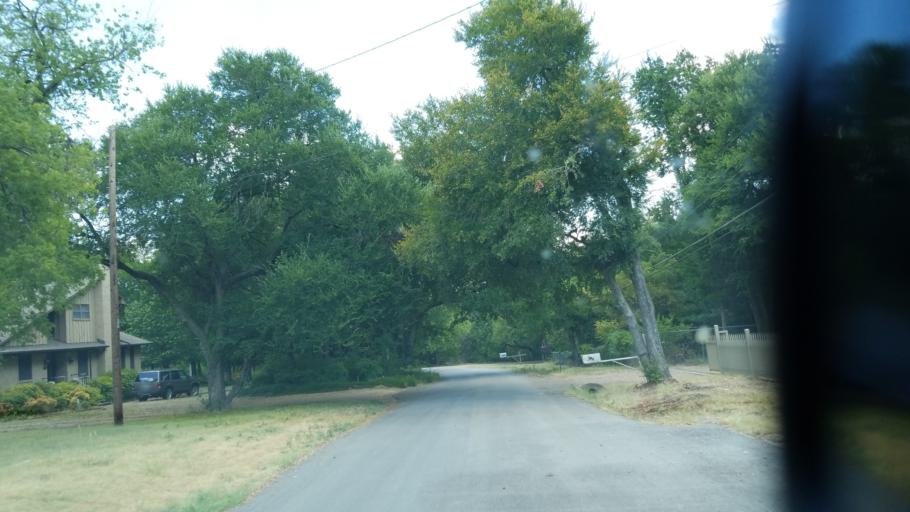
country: US
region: Texas
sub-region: Dallas County
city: Duncanville
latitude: 32.6730
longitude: -96.8873
